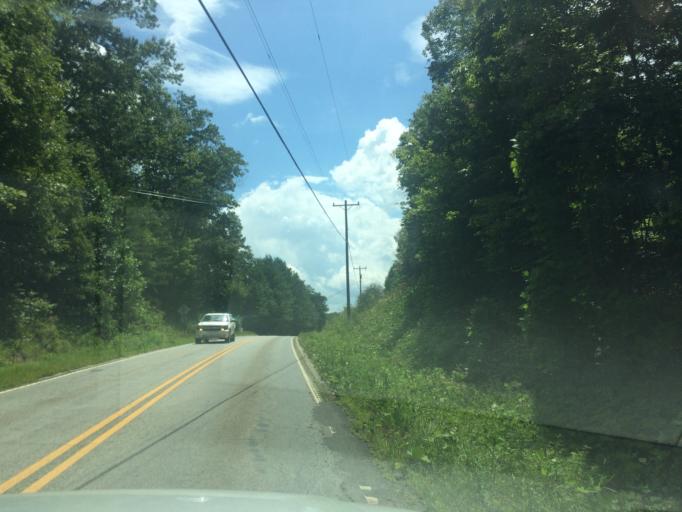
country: US
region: North Carolina
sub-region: Polk County
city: Columbus
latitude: 35.3194
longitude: -82.1776
